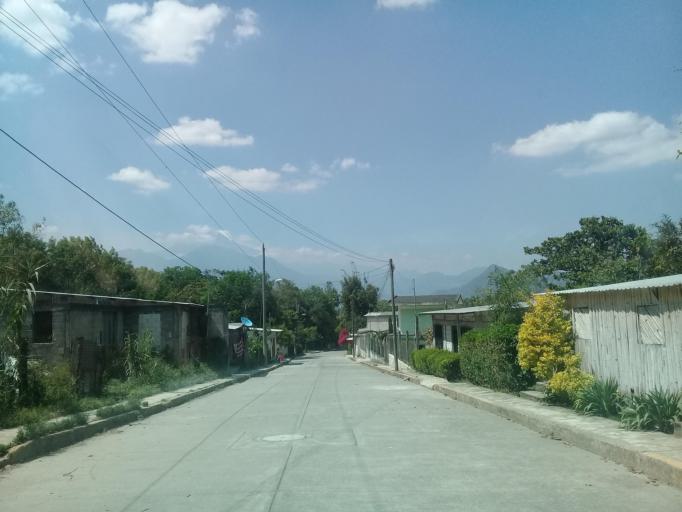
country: MX
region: Veracruz
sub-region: Tlilapan
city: Tonalixco
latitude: 18.8027
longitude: -97.0708
